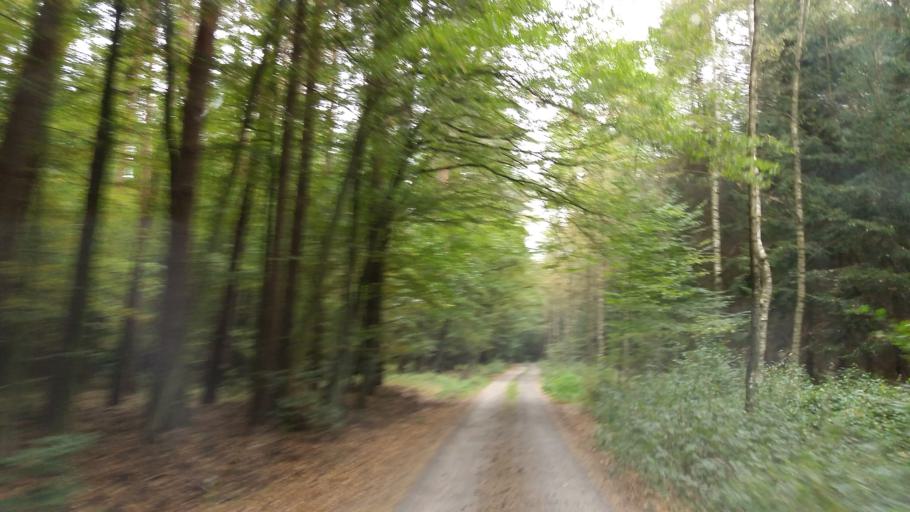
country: PL
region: West Pomeranian Voivodeship
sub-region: Powiat choszczenski
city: Pelczyce
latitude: 52.9632
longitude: 15.3197
